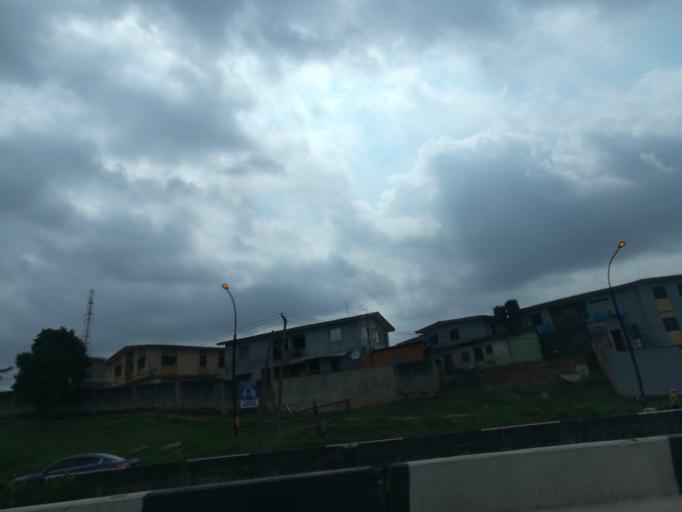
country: NG
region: Lagos
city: Somolu
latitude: 6.5527
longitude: 3.3970
